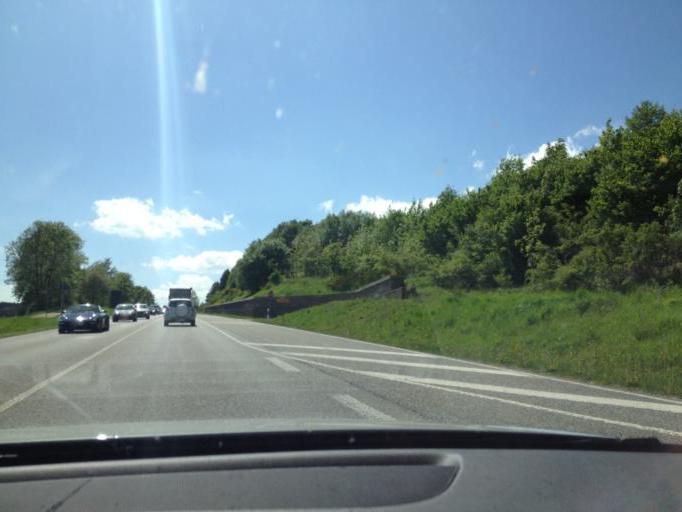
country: DE
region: Rheinland-Pfalz
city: Rommersheim
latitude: 50.2144
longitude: 6.4508
